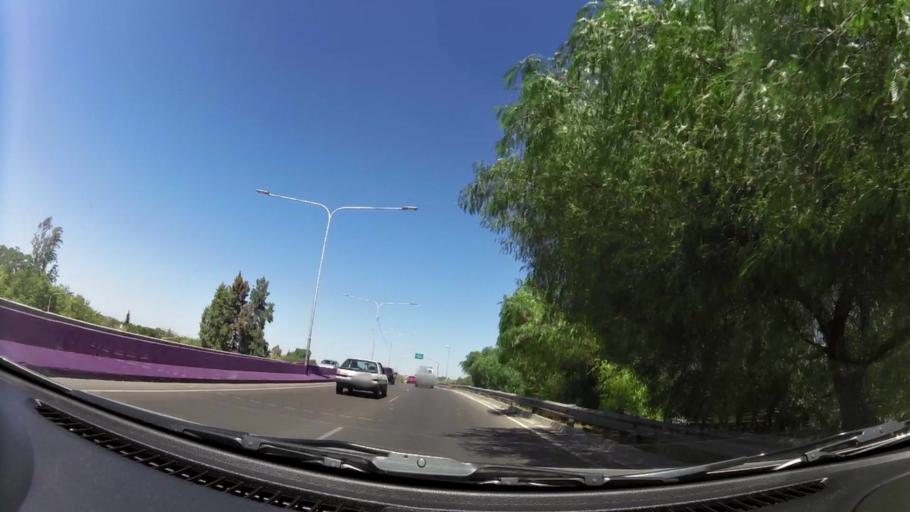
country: AR
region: Mendoza
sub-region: Departamento de Godoy Cruz
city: Godoy Cruz
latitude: -32.9284
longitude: -68.8642
